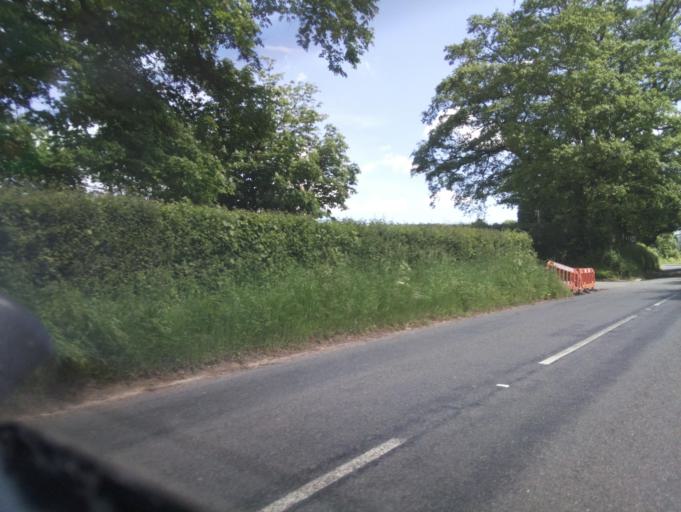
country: GB
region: Wales
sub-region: Monmouthshire
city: Monmouth
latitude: 51.8178
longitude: -2.7317
